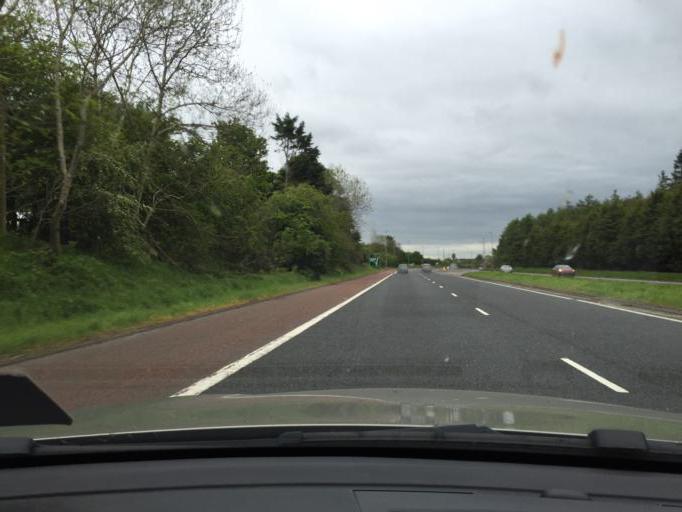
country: GB
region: Northern Ireland
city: Hillsborough
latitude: 54.4216
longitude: -6.1258
